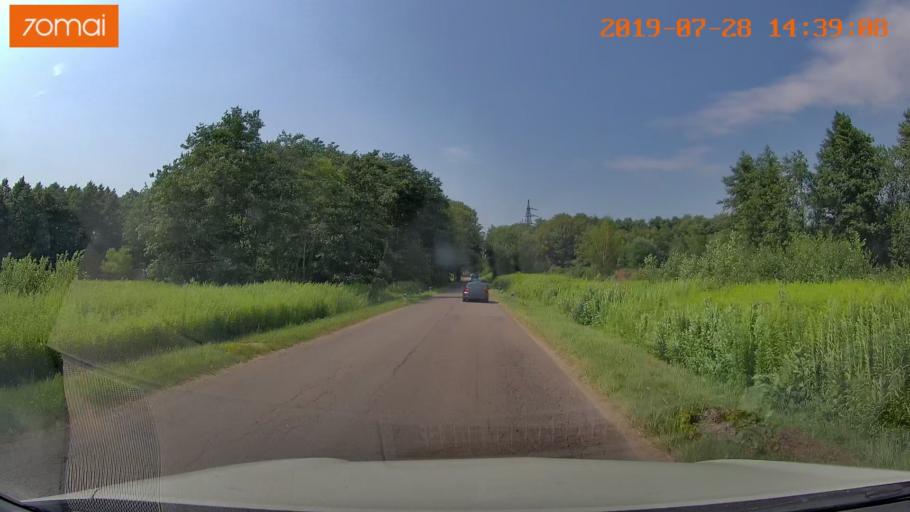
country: RU
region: Kaliningrad
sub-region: Gorod Kaliningrad
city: Yantarnyy
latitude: 54.8468
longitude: 19.9739
